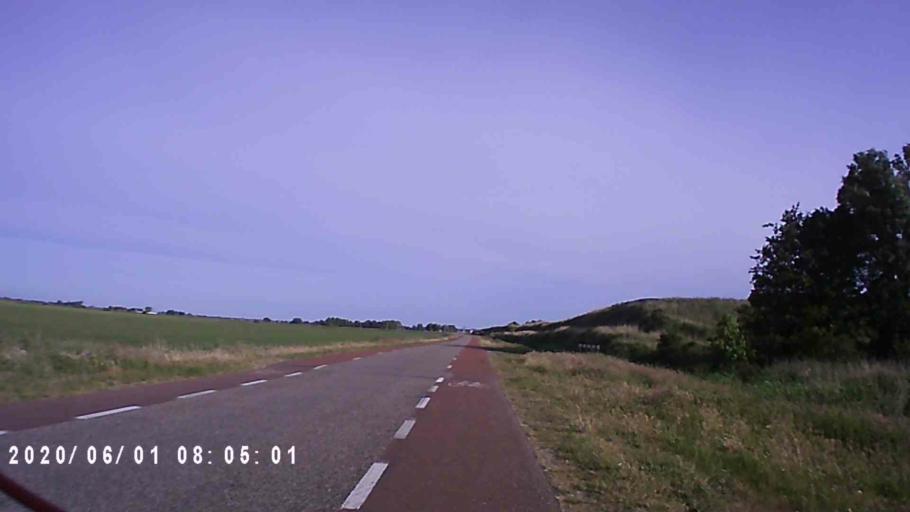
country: NL
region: Friesland
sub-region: Gemeente Tytsjerksteradiel
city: Oentsjerk
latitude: 53.2785
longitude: 5.9119
